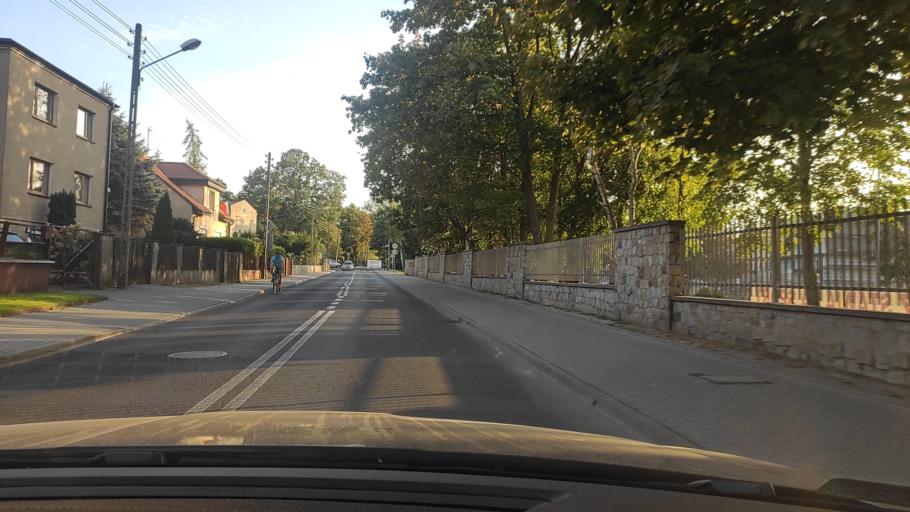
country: PL
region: Greater Poland Voivodeship
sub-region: Powiat poznanski
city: Swarzedz
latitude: 52.4112
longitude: 17.0718
